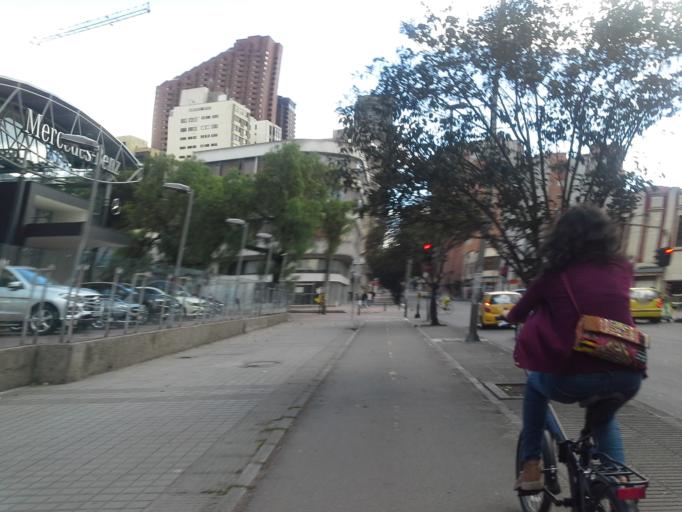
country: CO
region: Bogota D.C.
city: Bogota
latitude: 4.6224
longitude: -74.0680
